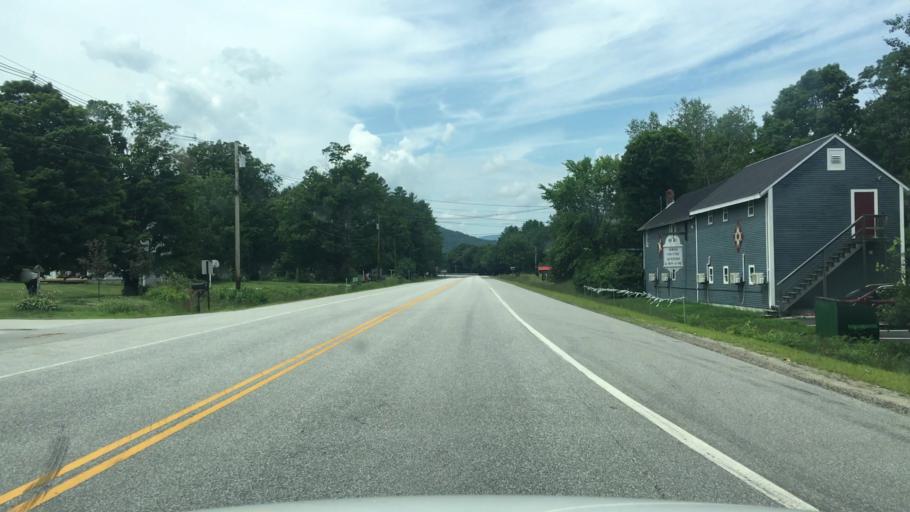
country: US
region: New Hampshire
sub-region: Grafton County
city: Rumney
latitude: 43.7949
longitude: -71.8175
